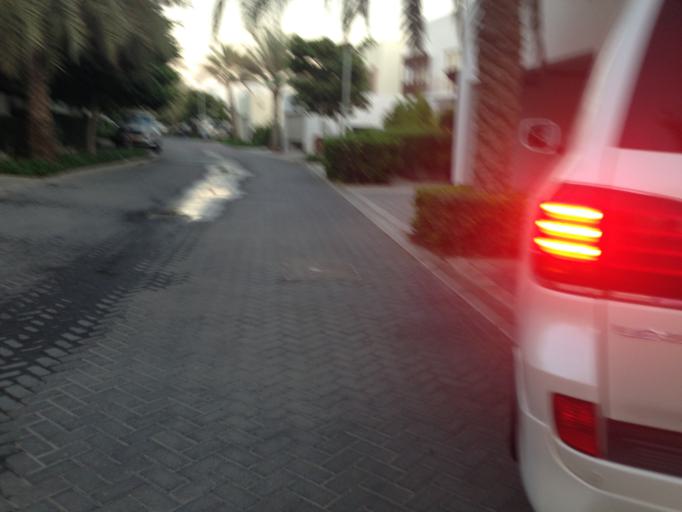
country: OM
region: Muhafazat Masqat
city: As Sib al Jadidah
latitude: 23.6253
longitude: 58.2658
